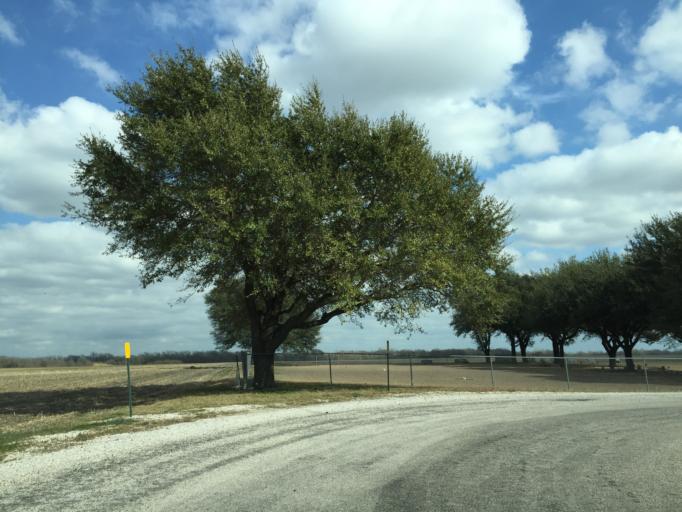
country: US
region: Texas
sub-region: Williamson County
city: Granger
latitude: 30.7116
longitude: -97.4732
